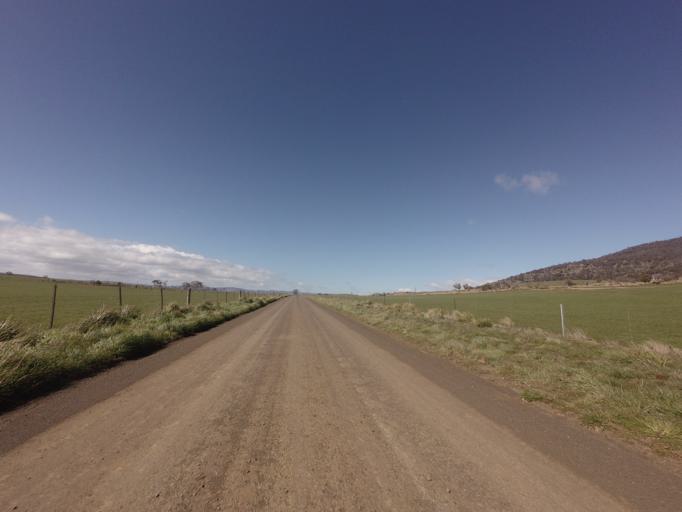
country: AU
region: Tasmania
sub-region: Northern Midlands
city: Evandale
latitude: -41.9213
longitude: 147.4004
